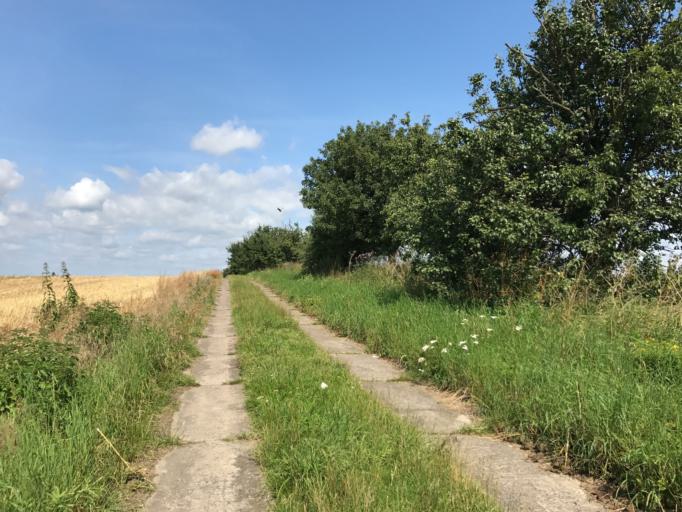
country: DE
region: Berlin
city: Karow
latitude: 52.6051
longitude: 13.5100
